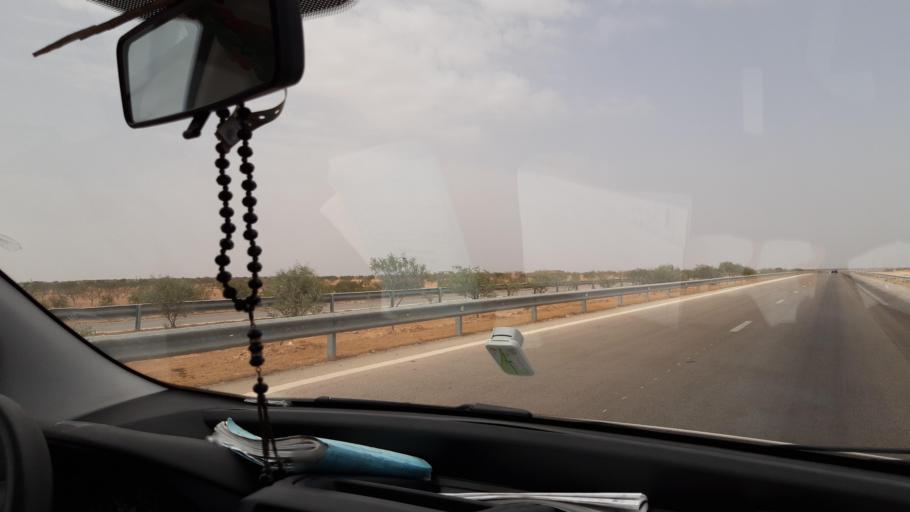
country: TN
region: Safaqis
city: Sfax
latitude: 34.8590
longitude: 10.6851
